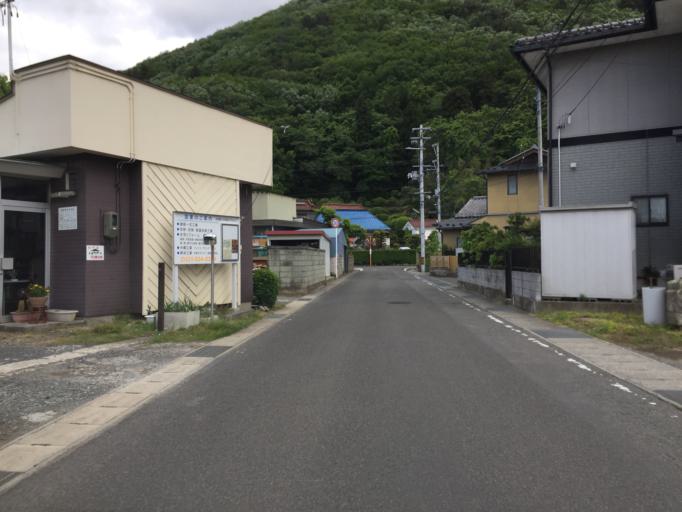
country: JP
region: Fukushima
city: Fukushima-shi
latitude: 37.7744
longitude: 140.4598
